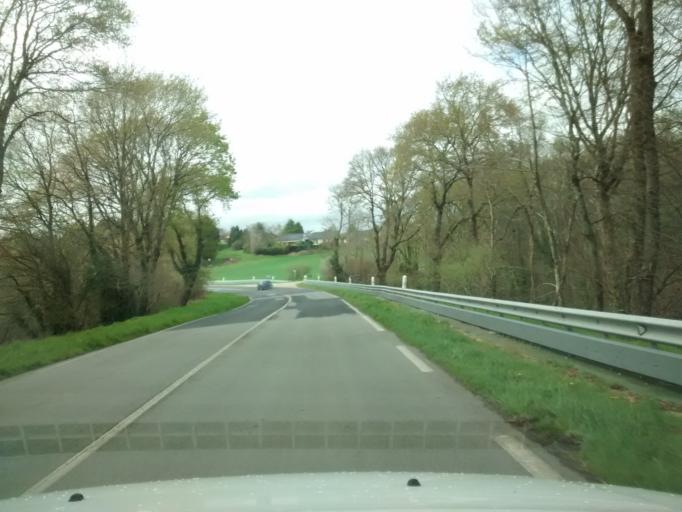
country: FR
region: Brittany
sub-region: Departement du Morbihan
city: Gestel
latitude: 47.7938
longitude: -3.4615
